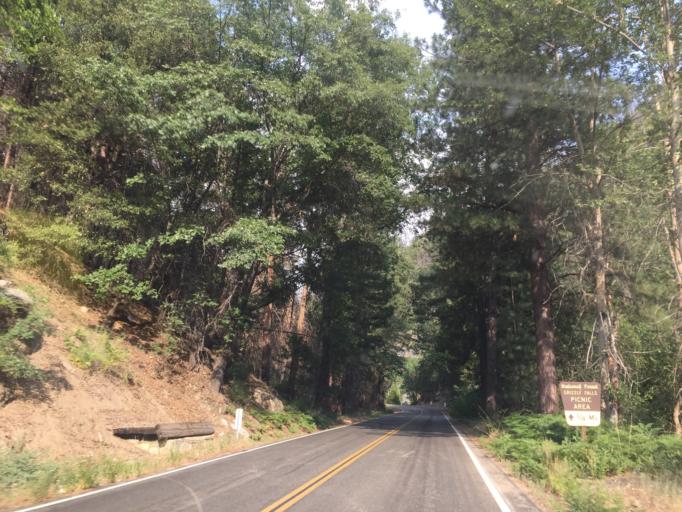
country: US
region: California
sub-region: Tulare County
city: Three Rivers
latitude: 36.8027
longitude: -118.7470
